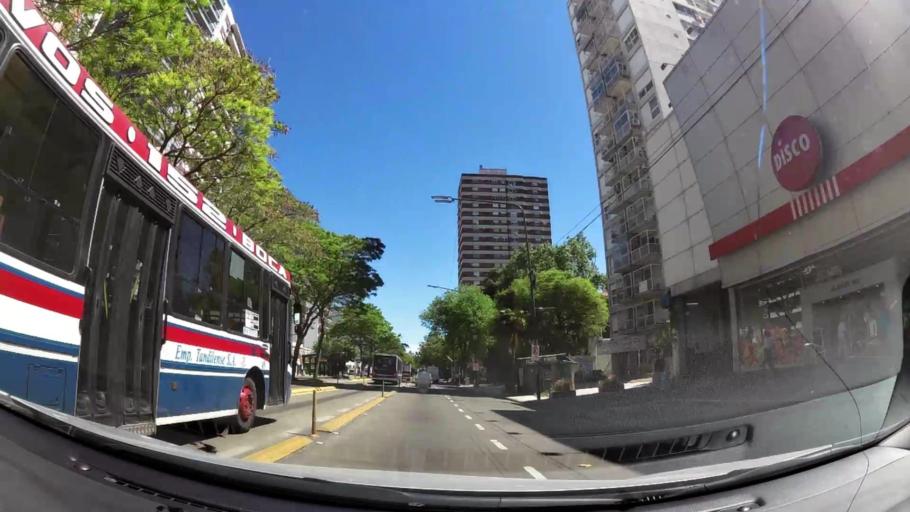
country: AR
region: Buenos Aires
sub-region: Partido de Vicente Lopez
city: Olivos
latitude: -34.5206
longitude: -58.4855
